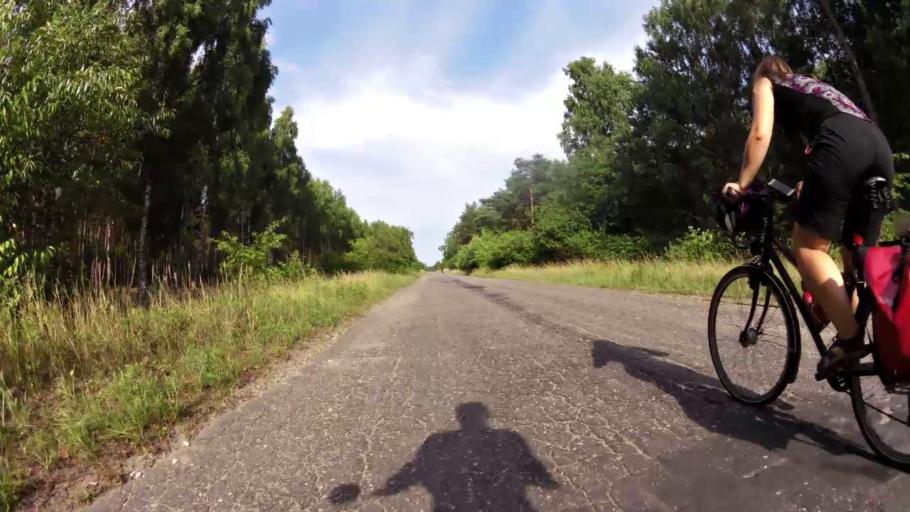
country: PL
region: West Pomeranian Voivodeship
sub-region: Powiat drawski
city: Drawsko Pomorskie
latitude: 53.4715
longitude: 15.7184
